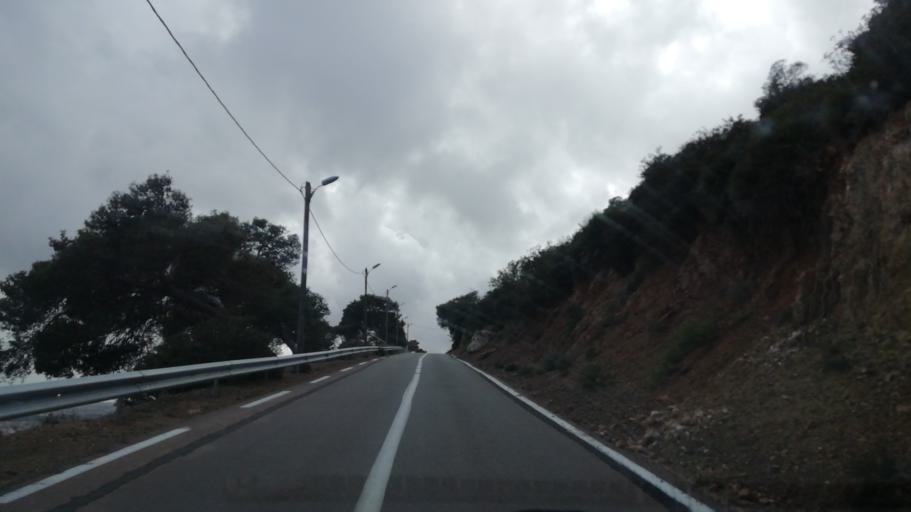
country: DZ
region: Oran
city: Oran
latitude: 35.7048
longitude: -0.6714
